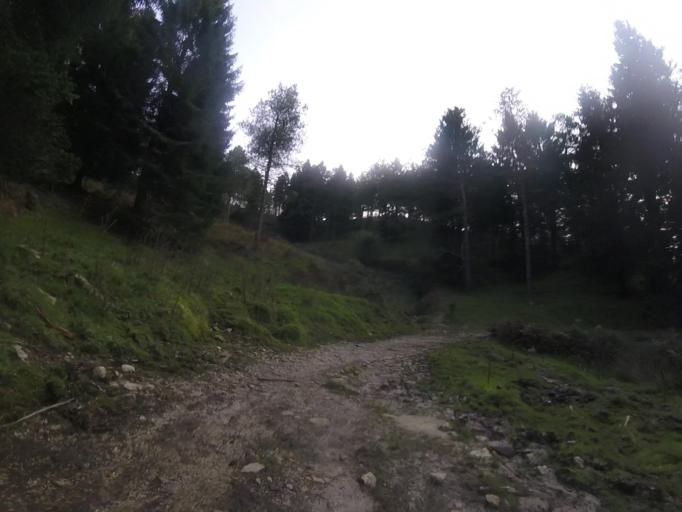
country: ES
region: Navarre
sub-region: Provincia de Navarra
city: Arano
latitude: 43.2453
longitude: -1.8288
